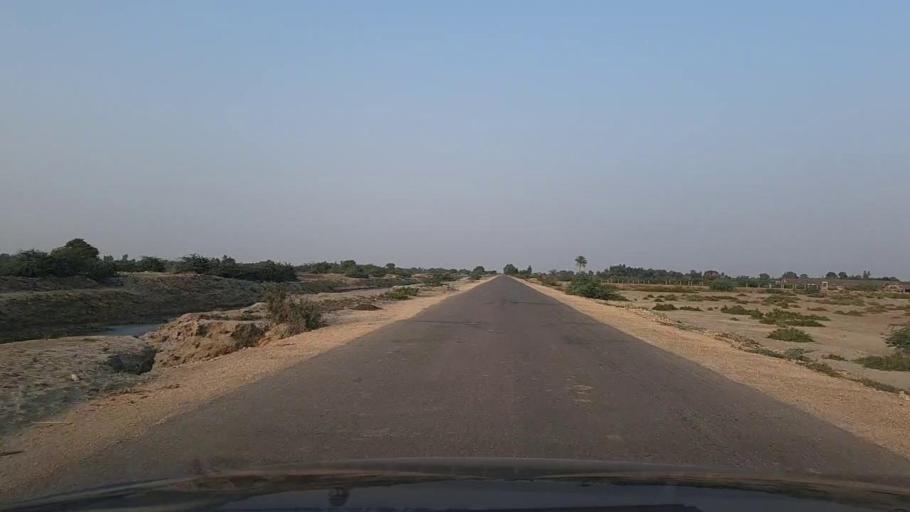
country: PK
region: Sindh
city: Mirpur Sakro
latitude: 24.4922
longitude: 67.8102
